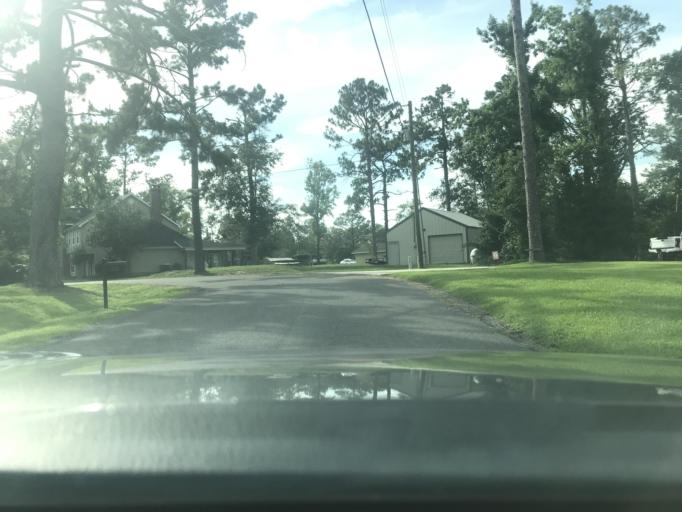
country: US
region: Louisiana
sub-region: Calcasieu Parish
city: Moss Bluff
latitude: 30.3348
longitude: -93.2603
